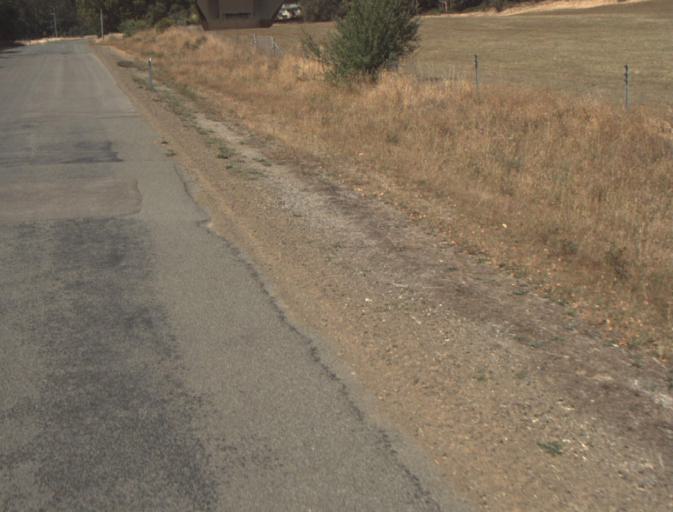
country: AU
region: Tasmania
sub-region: Dorset
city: Scottsdale
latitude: -41.3118
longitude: 147.3897
